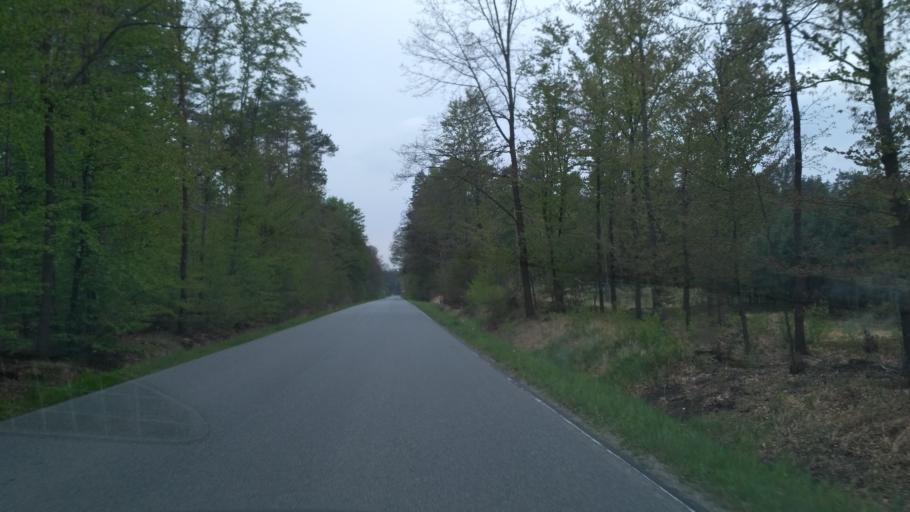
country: PL
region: Subcarpathian Voivodeship
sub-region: Powiat kolbuszowski
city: Kolbuszowa
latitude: 50.1535
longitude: 21.7585
